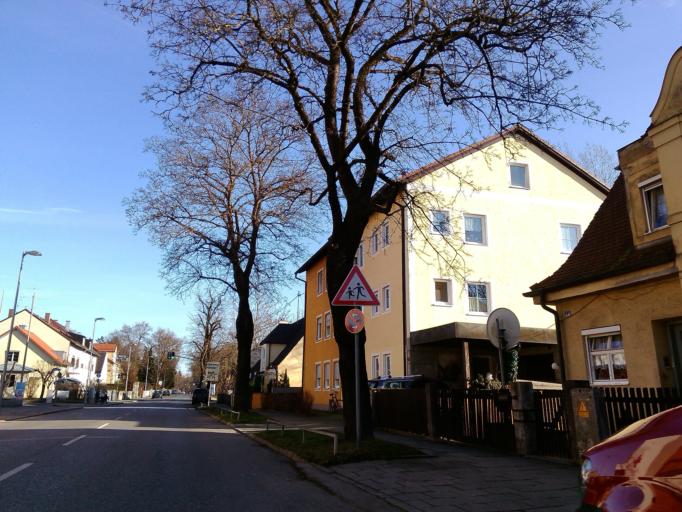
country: DE
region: Bavaria
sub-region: Upper Bavaria
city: Fuerstenfeldbruck
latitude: 48.1803
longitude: 11.2596
